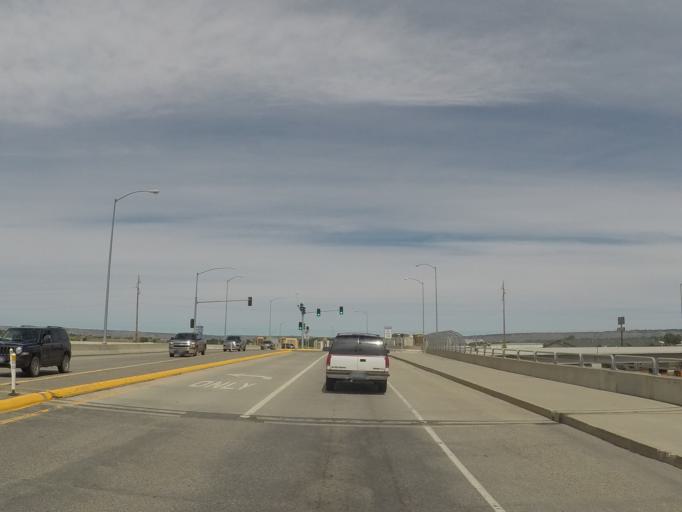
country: US
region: Montana
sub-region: Yellowstone County
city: Billings
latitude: 45.7318
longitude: -108.6034
